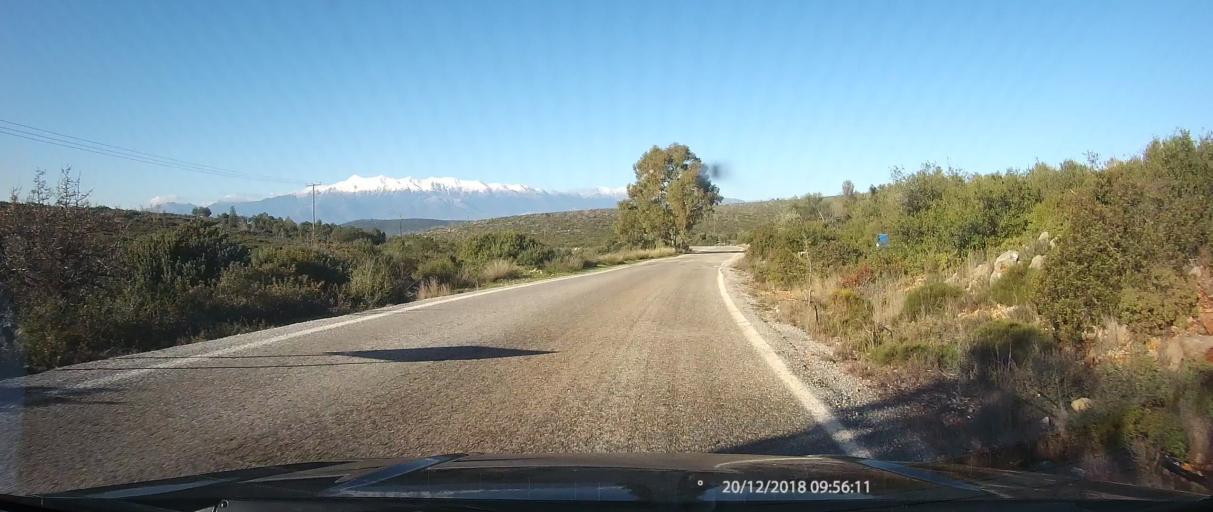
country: GR
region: Peloponnese
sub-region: Nomos Lakonias
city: Yerakion
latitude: 37.0224
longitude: 22.6155
